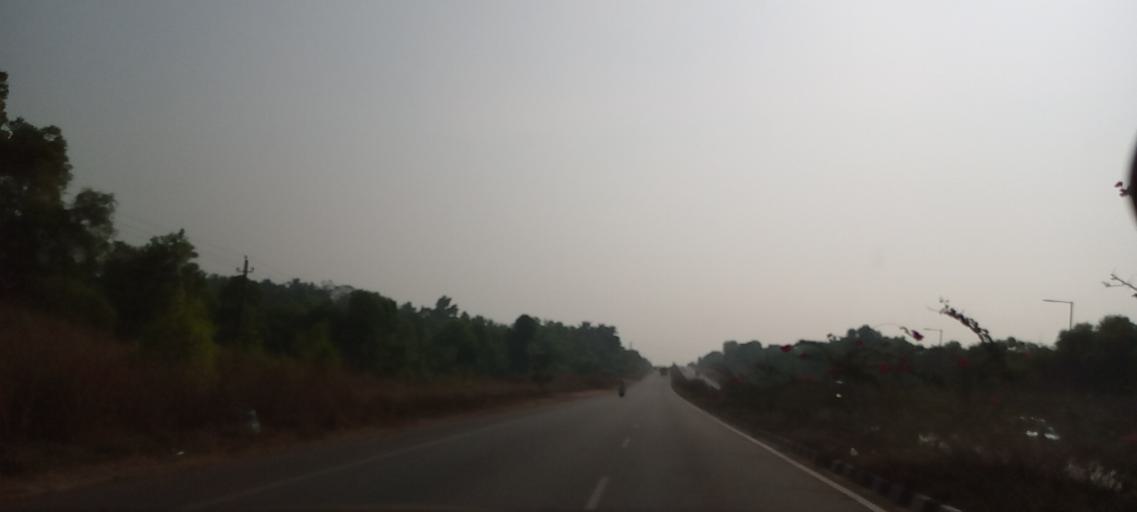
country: IN
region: Karnataka
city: Gangolli
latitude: 13.6883
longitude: 74.6632
